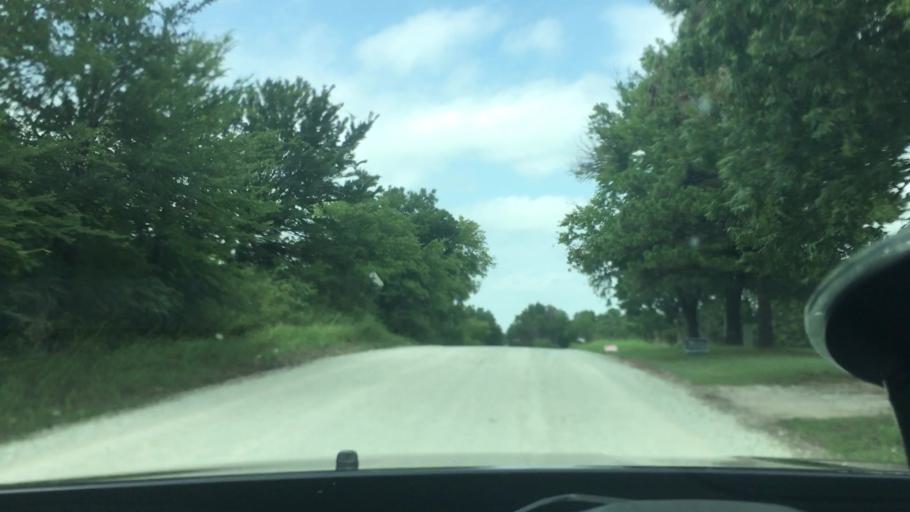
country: US
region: Oklahoma
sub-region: Pontotoc County
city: Ada
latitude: 34.8185
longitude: -96.7572
